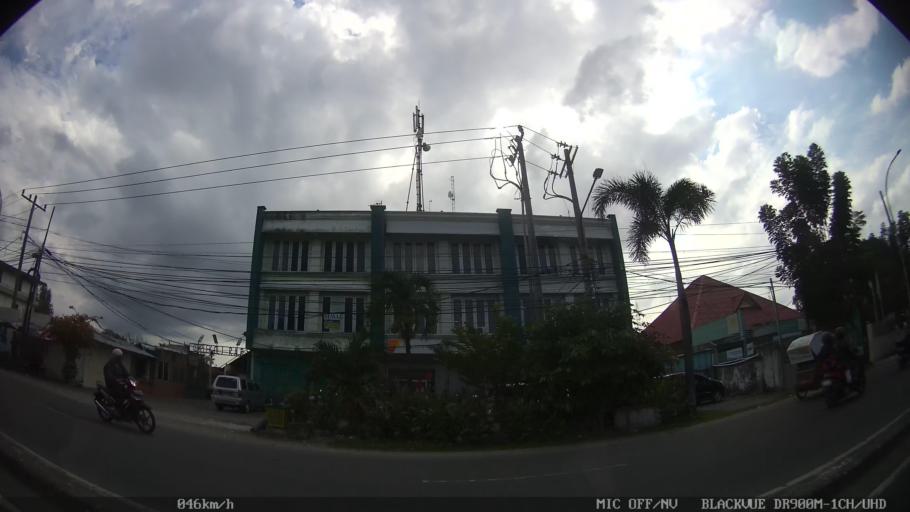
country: ID
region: North Sumatra
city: Medan
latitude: 3.6159
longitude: 98.6717
